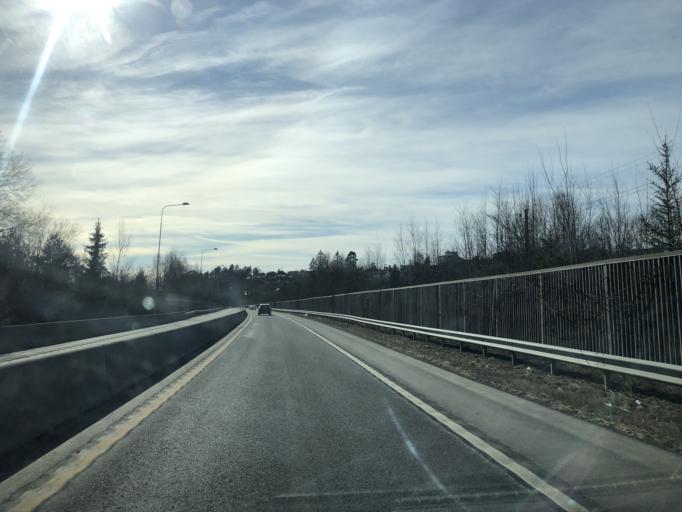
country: NO
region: Telemark
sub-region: Porsgrunn
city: Porsgrunn
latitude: 59.1130
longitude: 9.7000
